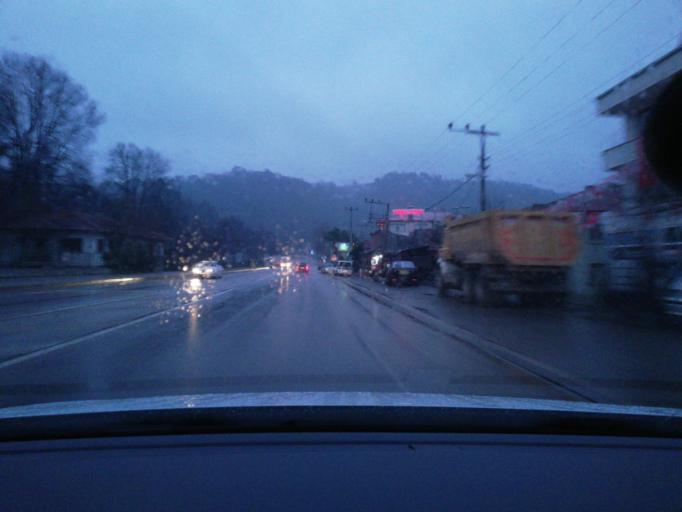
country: TR
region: Bolu
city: Bolu
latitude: 40.6893
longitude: 31.6201
